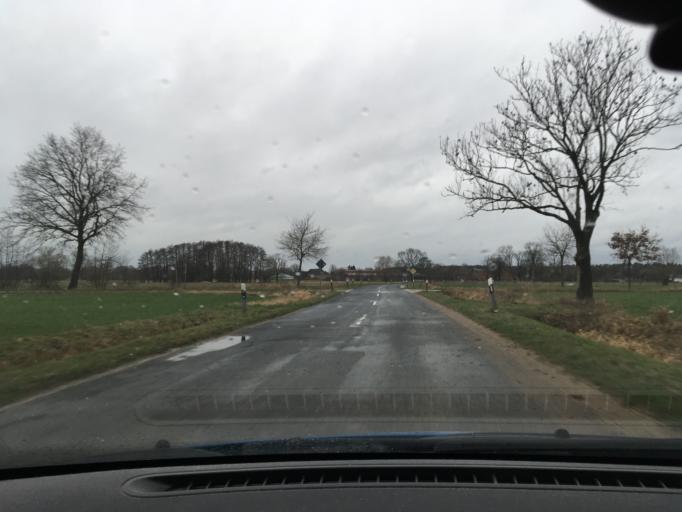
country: DE
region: Schleswig-Holstein
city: Lanze
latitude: 53.3634
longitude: 10.6377
